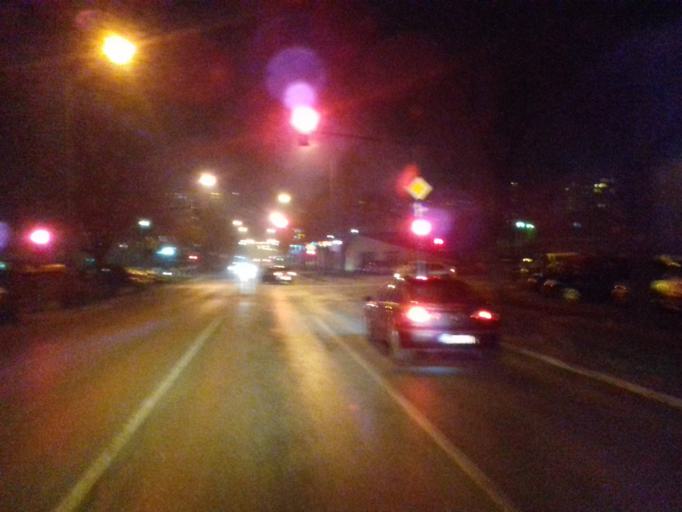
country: BA
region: Federation of Bosnia and Herzegovina
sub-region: Kanton Sarajevo
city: Sarajevo
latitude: 43.8489
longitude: 18.3865
